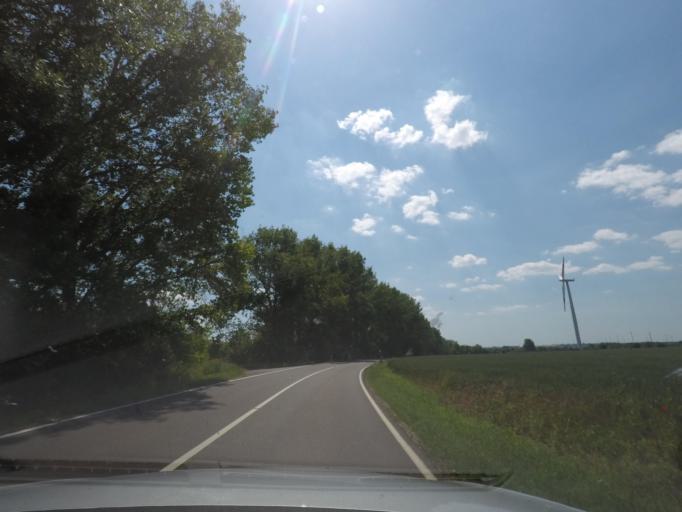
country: DE
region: Saxony-Anhalt
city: Eichenbarleben
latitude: 52.1920
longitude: 11.3761
